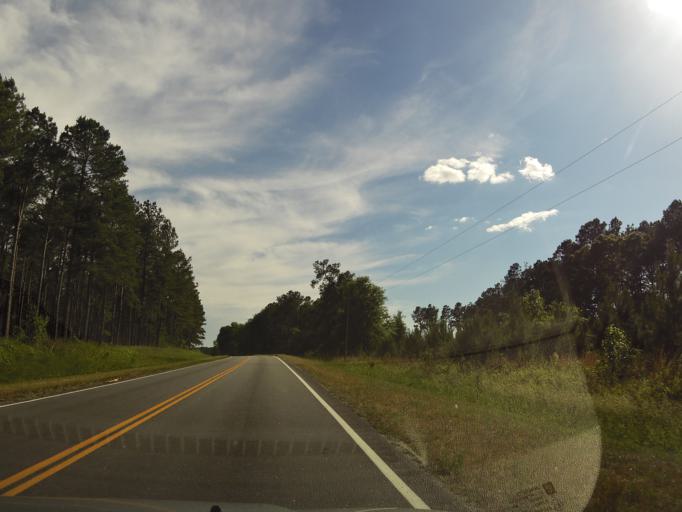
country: US
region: South Carolina
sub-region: Allendale County
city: Fairfax
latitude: 33.0109
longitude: -81.2170
